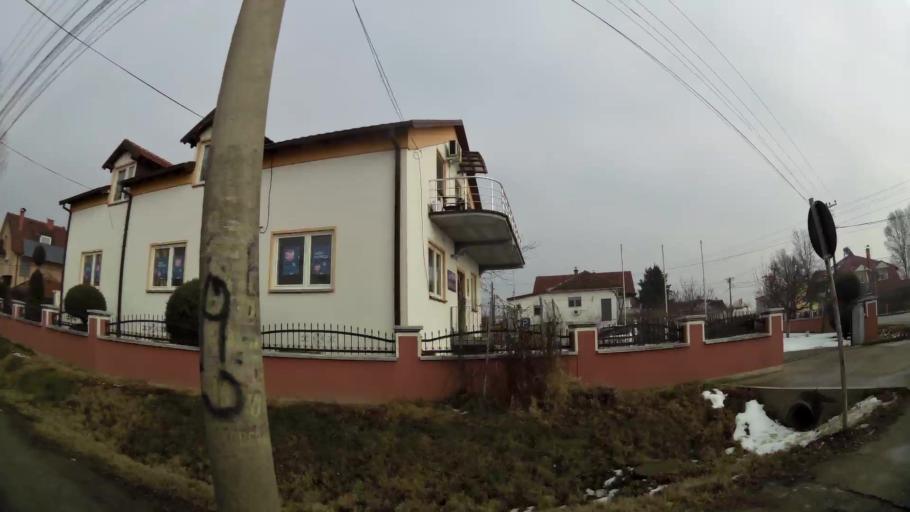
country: MK
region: Ilinden
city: Ilinden
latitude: 41.9919
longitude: 21.5808
